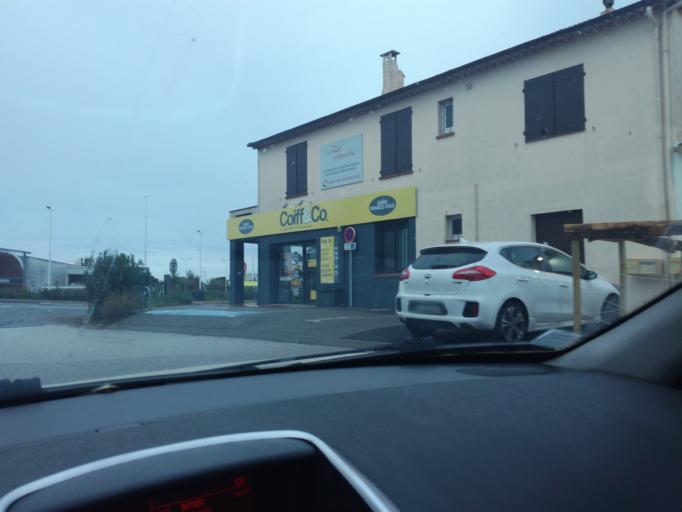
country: FR
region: Provence-Alpes-Cote d'Azur
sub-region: Departement du Var
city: Puget-sur-Argens
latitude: 43.4454
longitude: 6.6971
